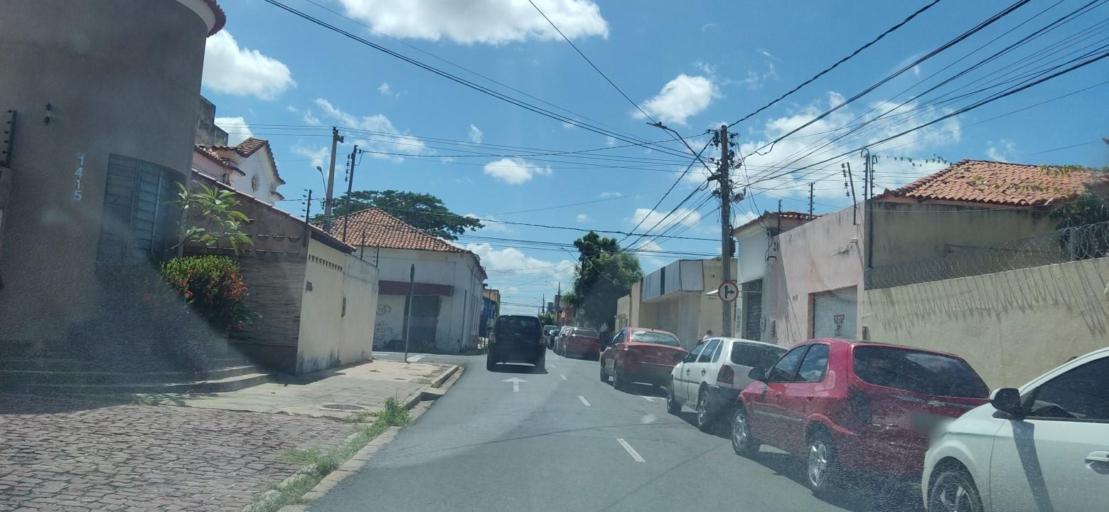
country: BR
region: Piaui
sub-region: Teresina
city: Teresina
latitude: -5.0864
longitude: -42.8147
